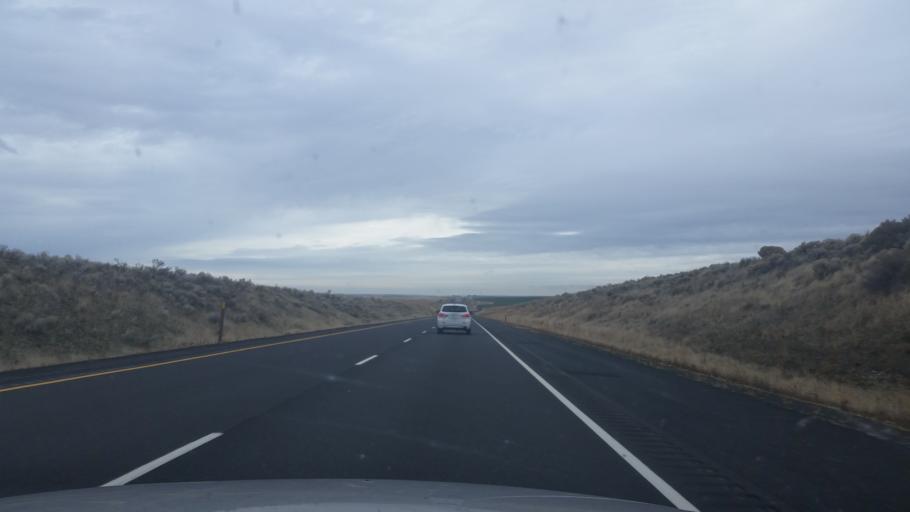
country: US
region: Washington
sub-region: Grant County
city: Warden
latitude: 47.0865
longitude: -118.7299
